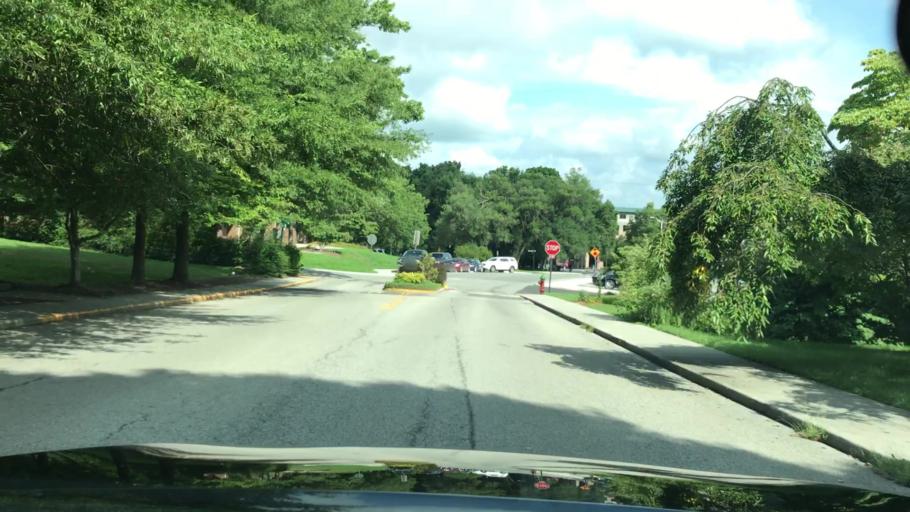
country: US
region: Virginia
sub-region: Montgomery County
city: Blacksburg
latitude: 37.2256
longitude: -80.4117
